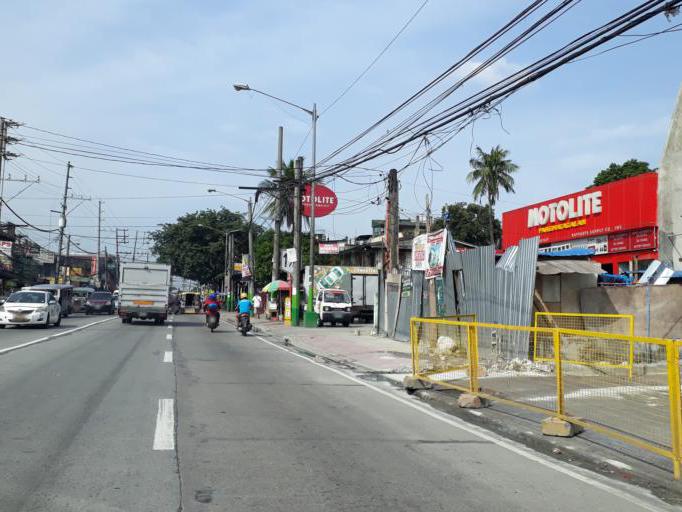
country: PH
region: Calabarzon
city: Bagong Pagasa
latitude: 14.6680
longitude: 121.0084
